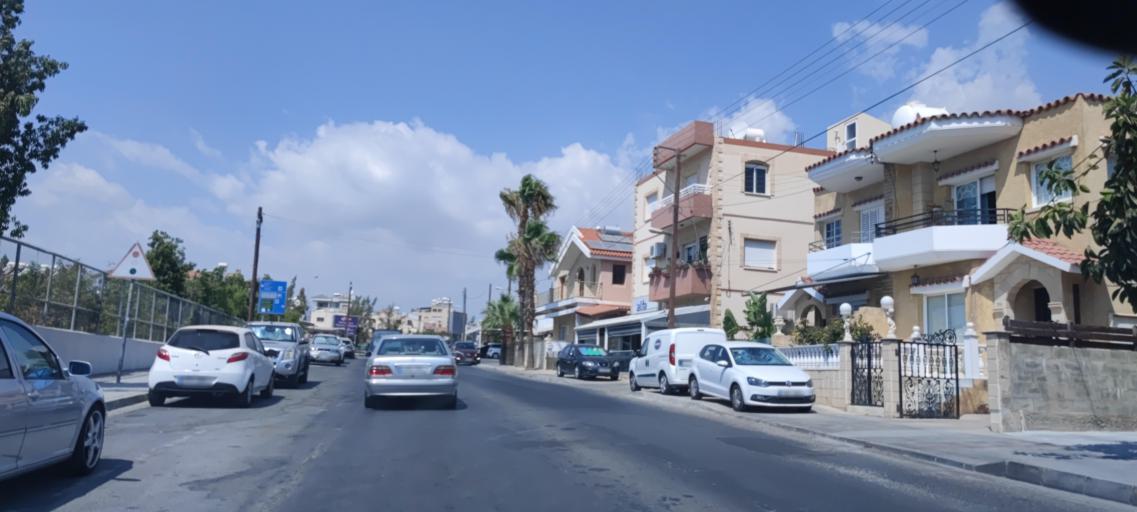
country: CY
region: Limassol
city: Limassol
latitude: 34.6941
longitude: 33.0301
